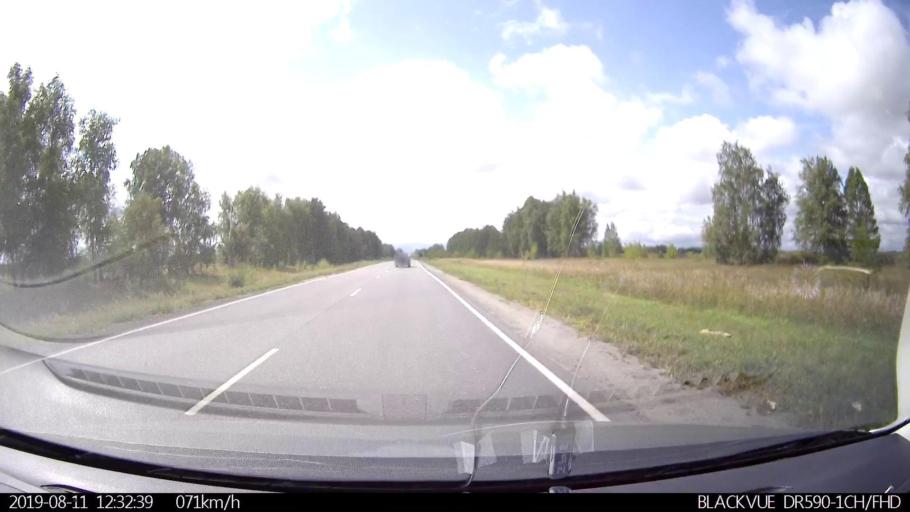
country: RU
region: Ulyanovsk
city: Ignatovka
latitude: 53.8123
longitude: 47.8638
